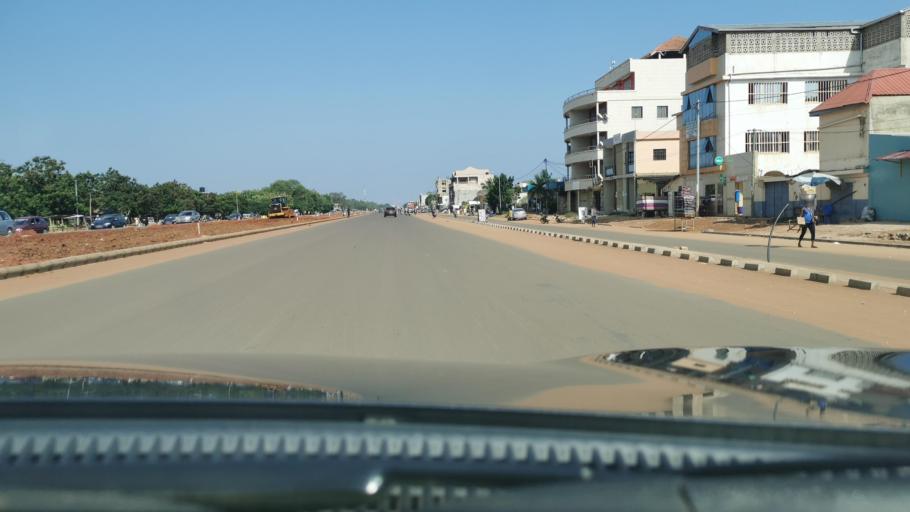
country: TG
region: Maritime
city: Lome
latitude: 6.1977
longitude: 1.1520
